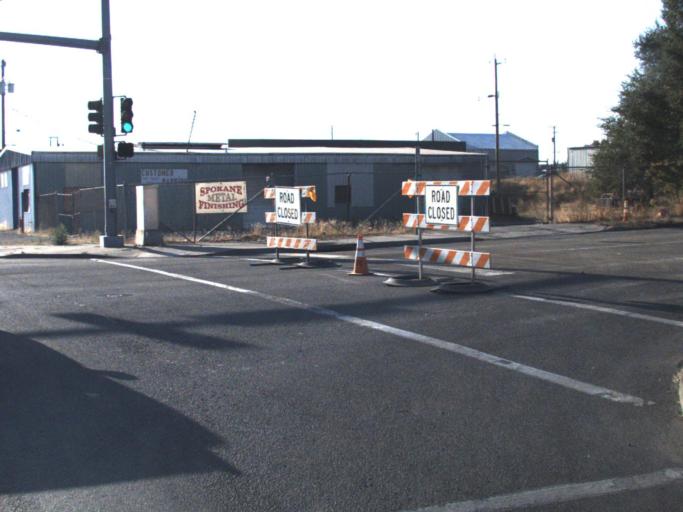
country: US
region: Washington
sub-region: Spokane County
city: Spokane
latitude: 47.6619
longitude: -117.3870
